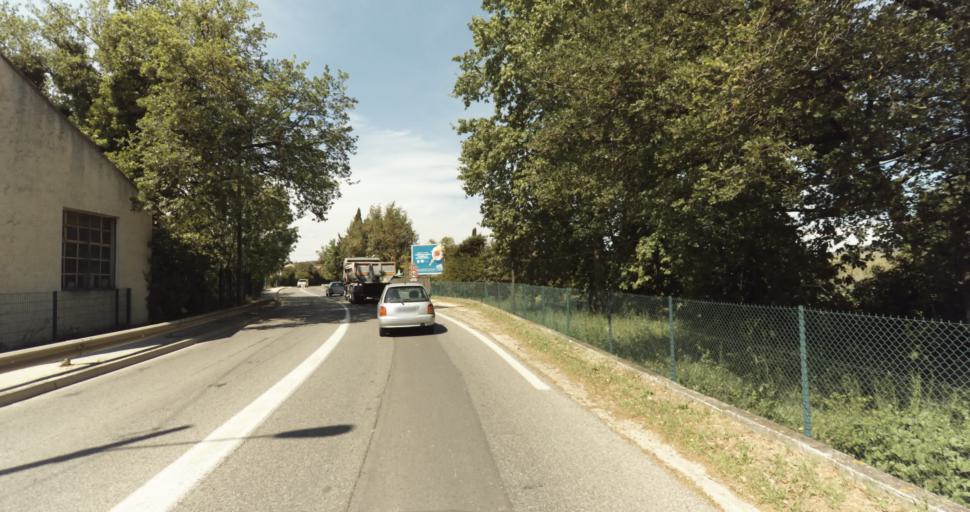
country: FR
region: Provence-Alpes-Cote d'Azur
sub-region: Departement du Var
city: Hyeres
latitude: 43.1249
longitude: 6.1549
